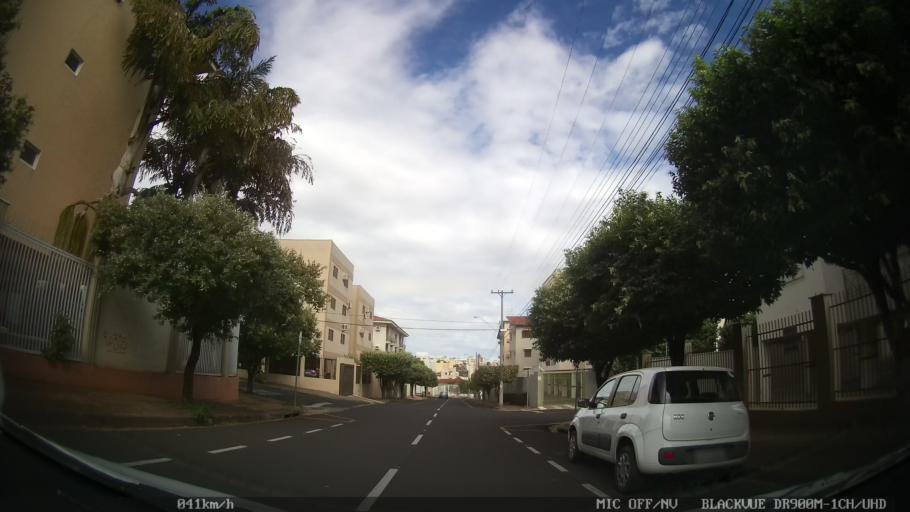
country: BR
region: Sao Paulo
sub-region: Sao Jose Do Rio Preto
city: Sao Jose do Rio Preto
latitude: -20.8310
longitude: -49.3828
